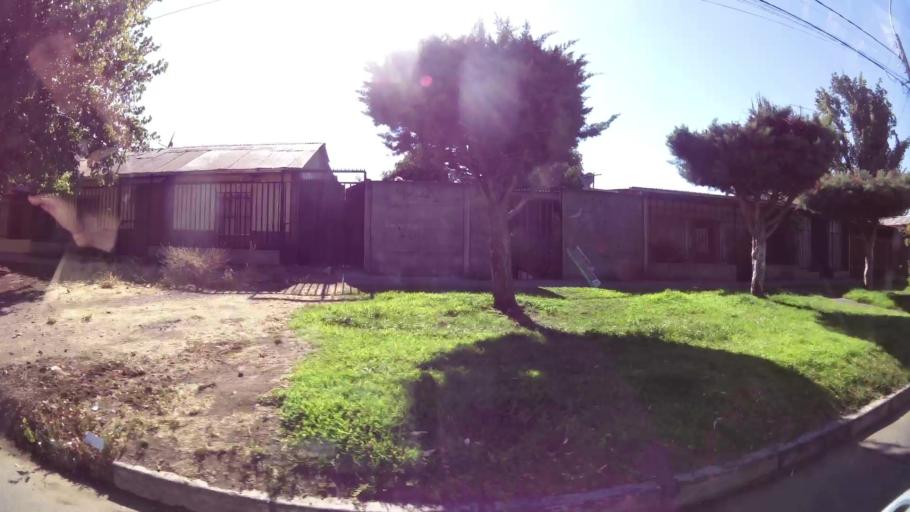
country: CL
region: Maule
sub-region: Provincia de Curico
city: Curico
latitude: -34.9954
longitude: -71.2458
